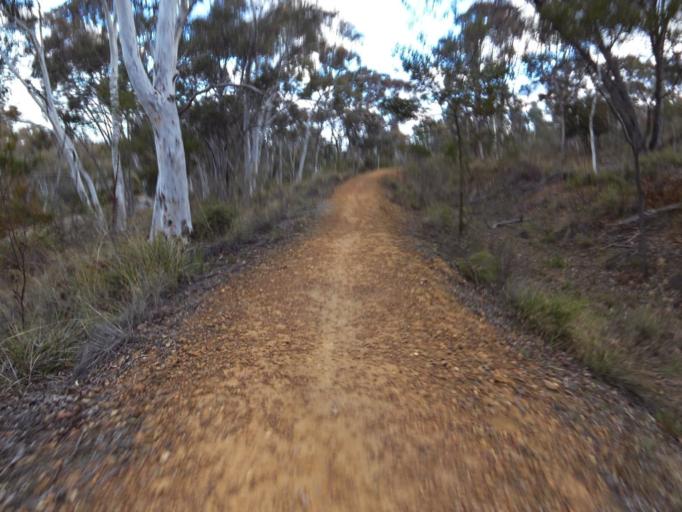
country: AU
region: Australian Capital Territory
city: Acton
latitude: -35.2674
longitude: 149.1096
